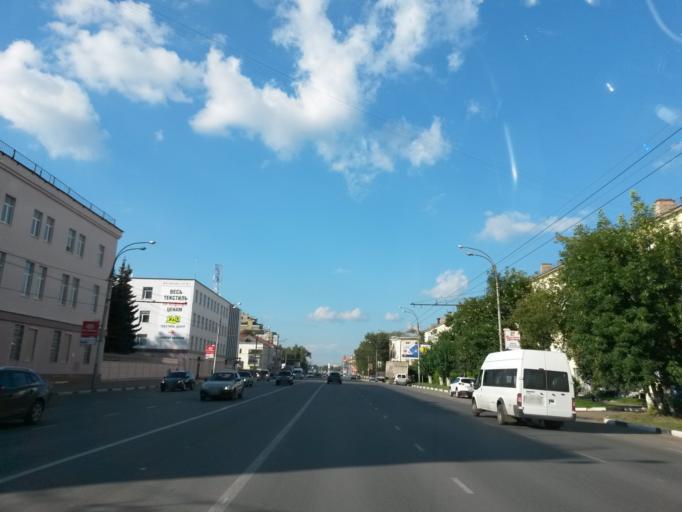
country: RU
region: Ivanovo
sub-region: Gorod Ivanovo
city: Ivanovo
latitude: 56.9767
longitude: 40.9761
